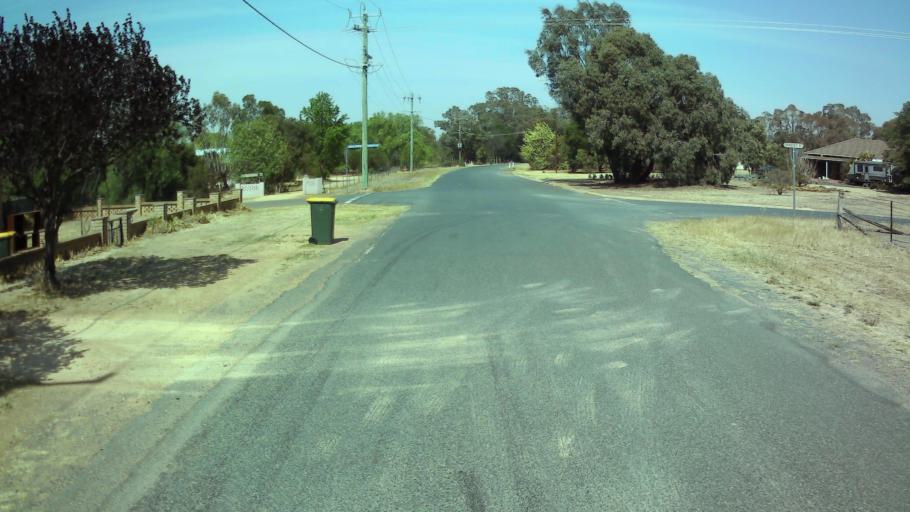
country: AU
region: New South Wales
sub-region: Weddin
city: Grenfell
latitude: -33.8948
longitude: 148.1513
